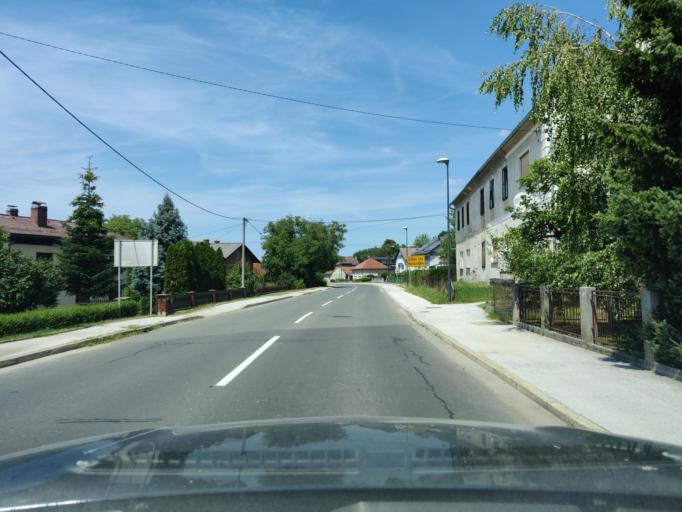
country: SI
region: Lendava-Lendva
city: Lendava
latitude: 46.5746
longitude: 16.4474
